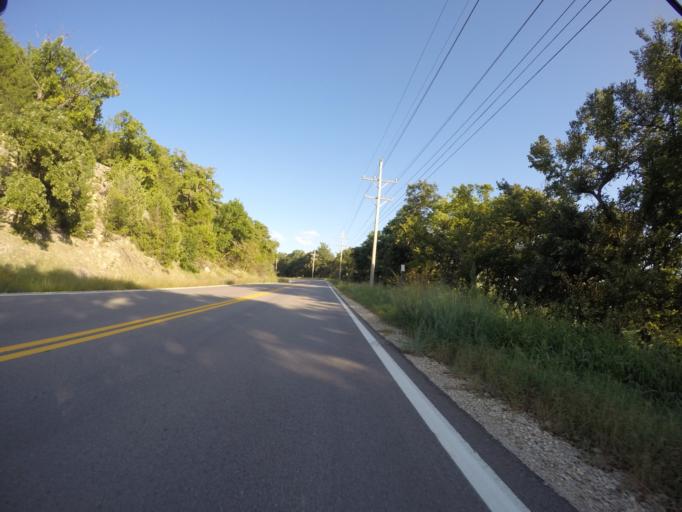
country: US
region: Kansas
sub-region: Riley County
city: Manhattan
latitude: 39.1574
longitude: -96.6195
